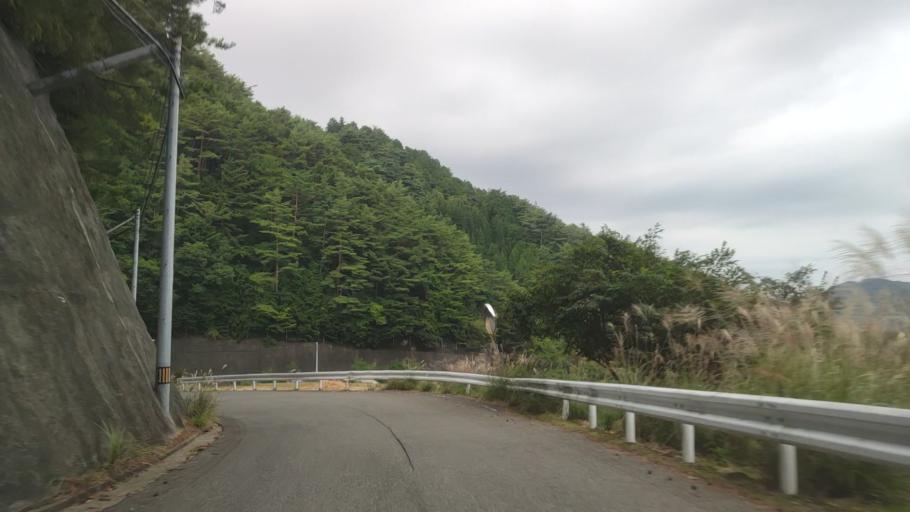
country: JP
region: Wakayama
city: Koya
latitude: 34.2231
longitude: 135.6146
